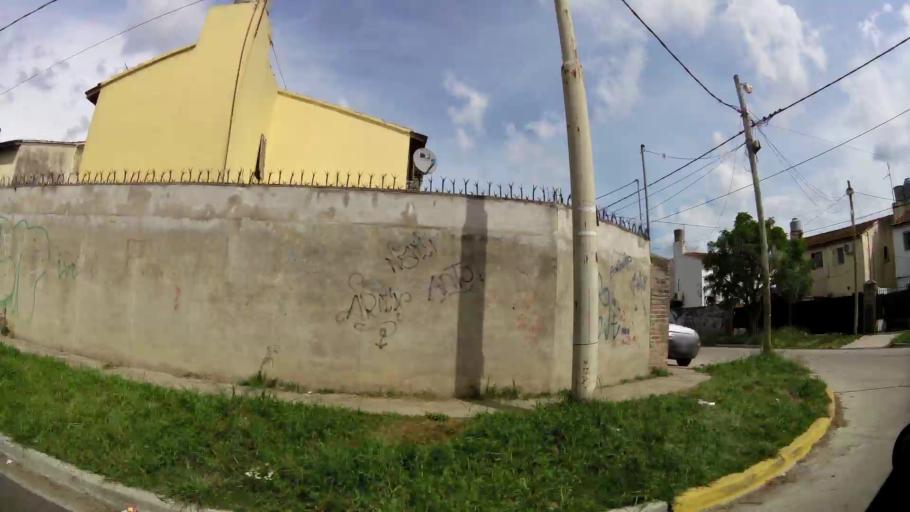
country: AR
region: Buenos Aires
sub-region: Partido de Quilmes
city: Quilmes
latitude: -34.7609
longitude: -58.2491
